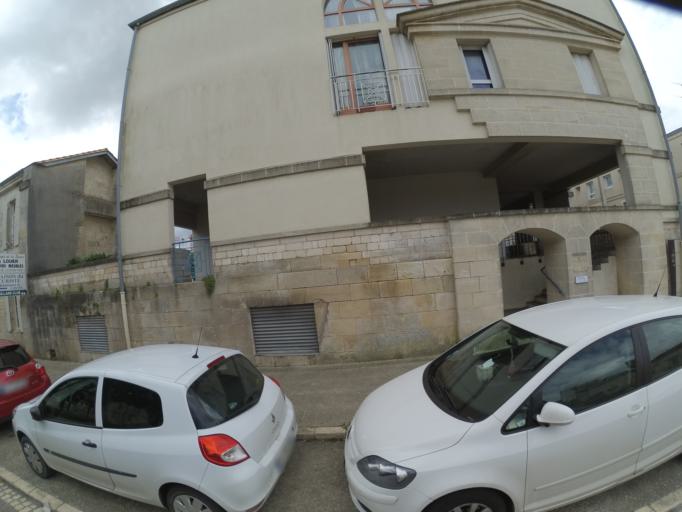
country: FR
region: Poitou-Charentes
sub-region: Departement de la Charente-Maritime
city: Rochefort
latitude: 45.9426
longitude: -0.9597
